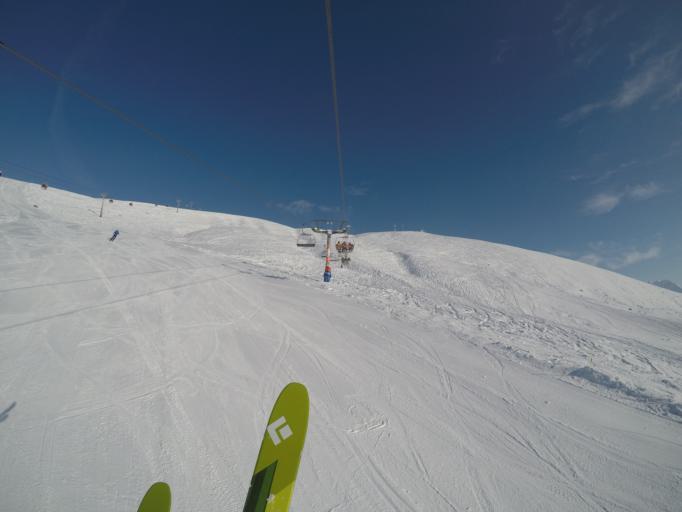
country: GE
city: Gudauri
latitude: 42.4824
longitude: 44.4945
